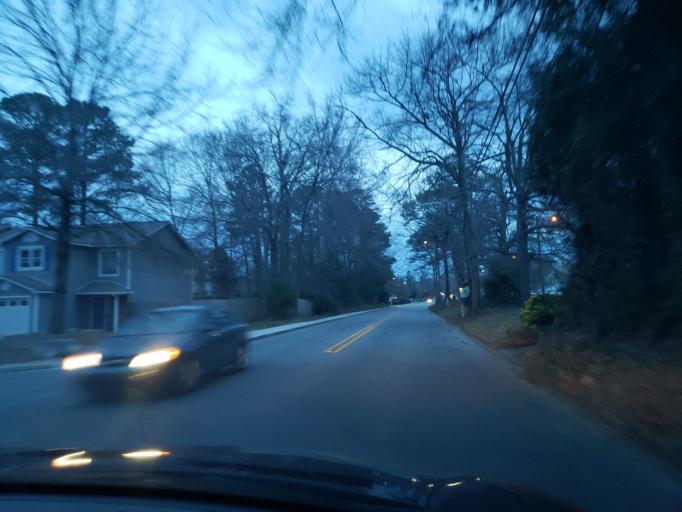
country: US
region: Alabama
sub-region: Lee County
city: Auburn
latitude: 32.6156
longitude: -85.4797
